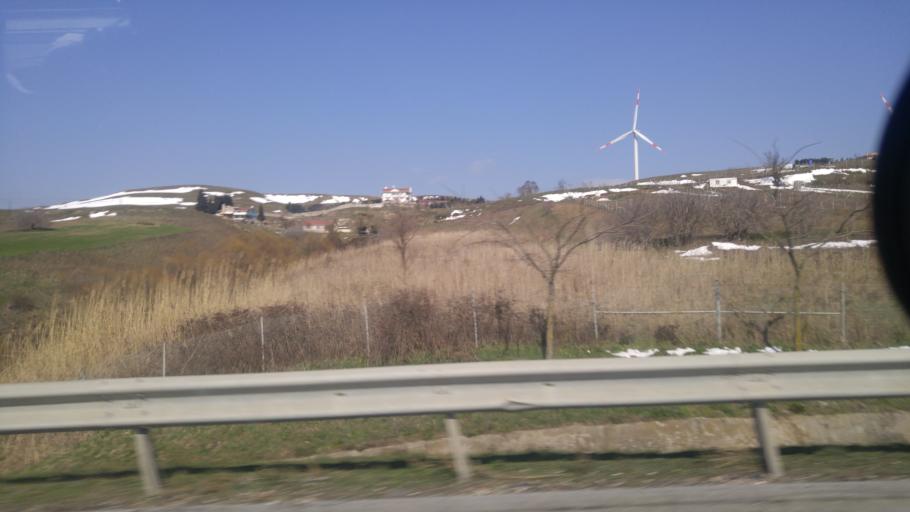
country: TR
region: Istanbul
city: Celaliye
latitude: 41.0512
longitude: 28.4378
